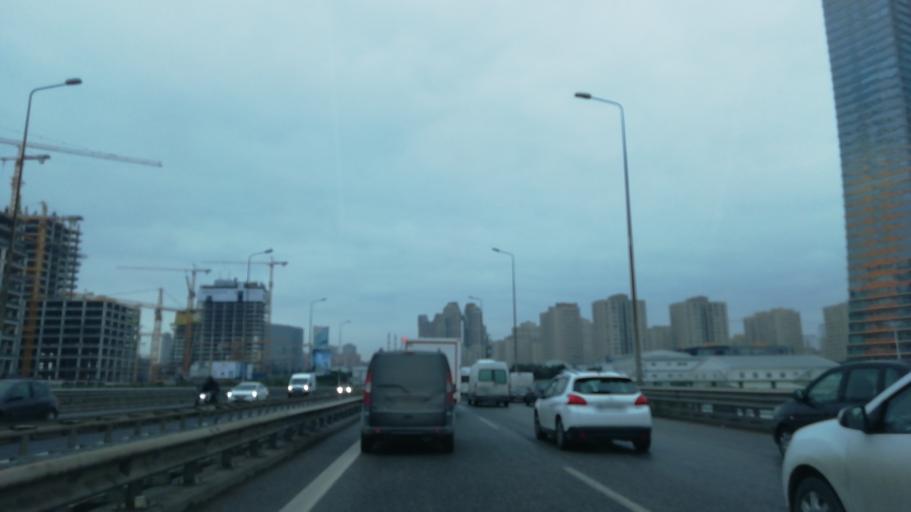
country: TR
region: Istanbul
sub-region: Atasehir
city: Atasehir
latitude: 41.0032
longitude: 29.1029
